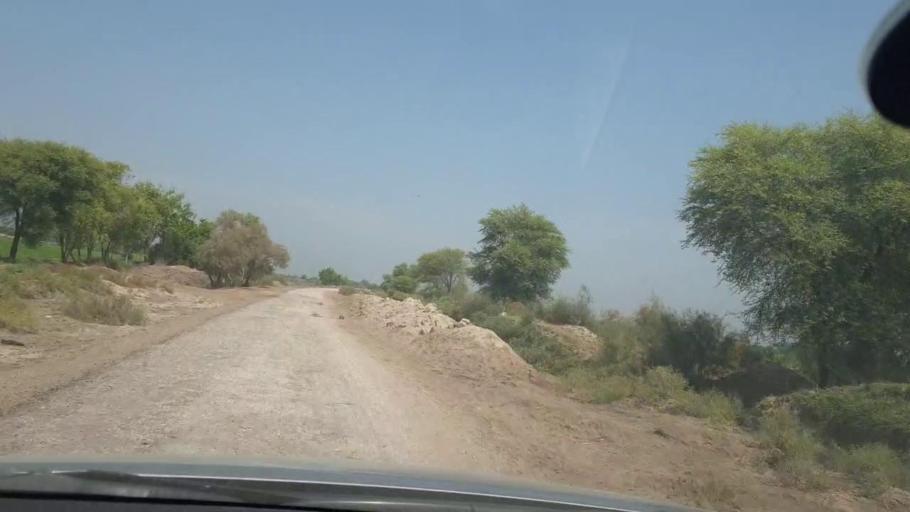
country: PK
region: Balochistan
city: Mehrabpur
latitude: 28.0804
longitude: 68.0425
